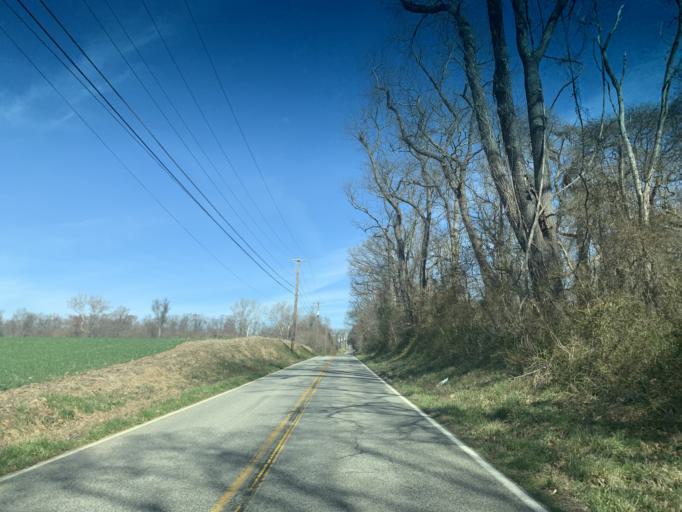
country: US
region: Maryland
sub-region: Cecil County
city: Charlestown
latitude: 39.5501
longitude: -76.0107
